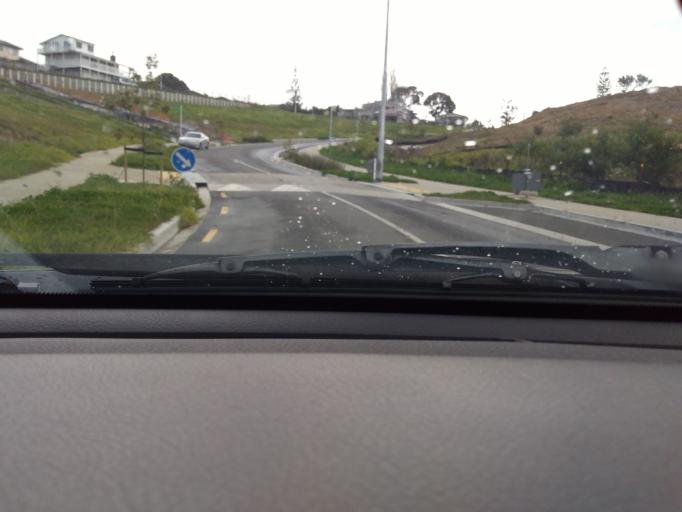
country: NZ
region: Auckland
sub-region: Auckland
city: Rosebank
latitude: -36.8291
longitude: 174.6139
